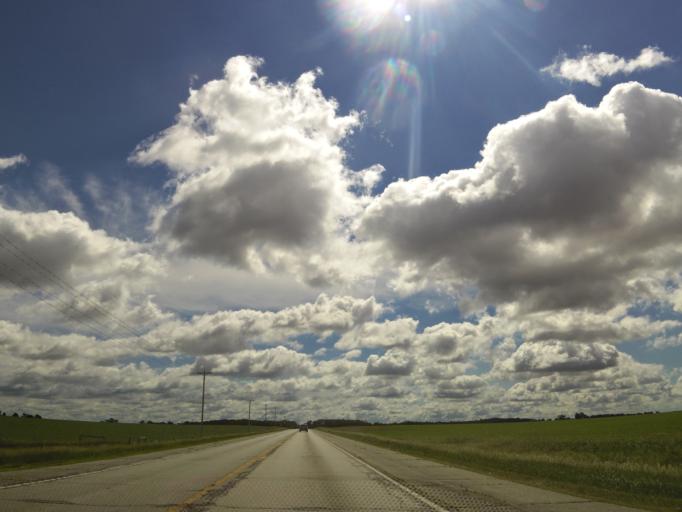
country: US
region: Minnesota
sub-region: Fillmore County
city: Spring Valley
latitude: 43.7107
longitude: -92.4657
